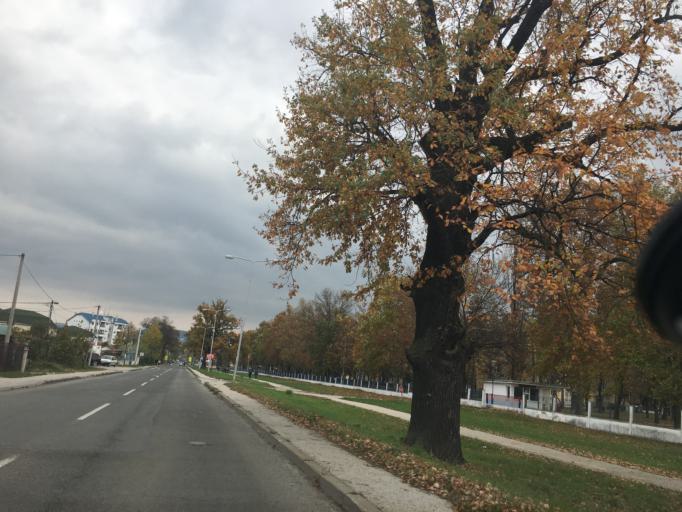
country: RS
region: Central Serbia
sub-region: Raski Okrug
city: Kraljevo
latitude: 43.7138
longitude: 20.6782
